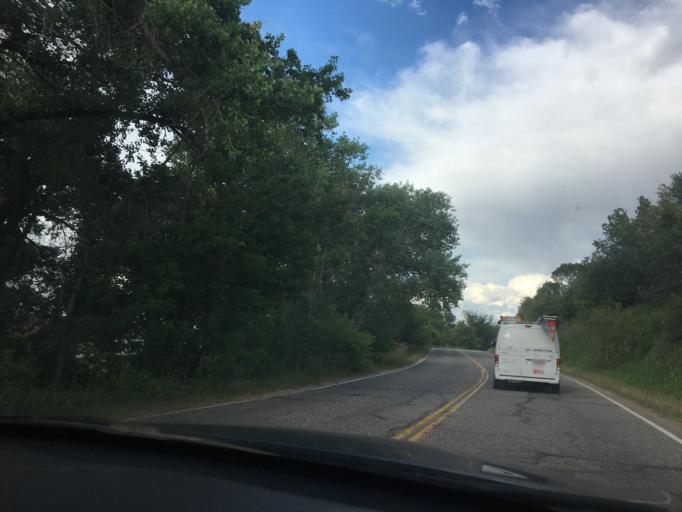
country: US
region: Colorado
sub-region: Jefferson County
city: Applewood
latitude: 39.7661
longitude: -105.1913
